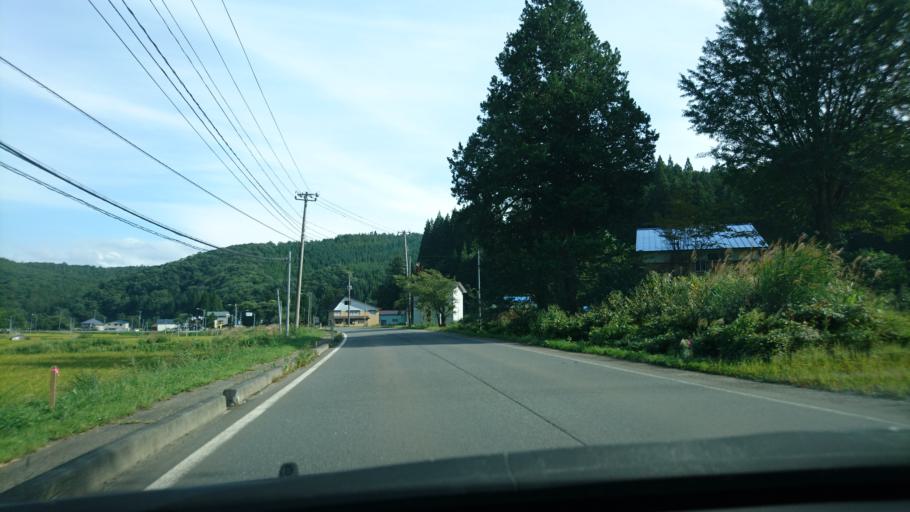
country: JP
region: Akita
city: Yokotemachi
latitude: 39.3120
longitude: 140.7590
